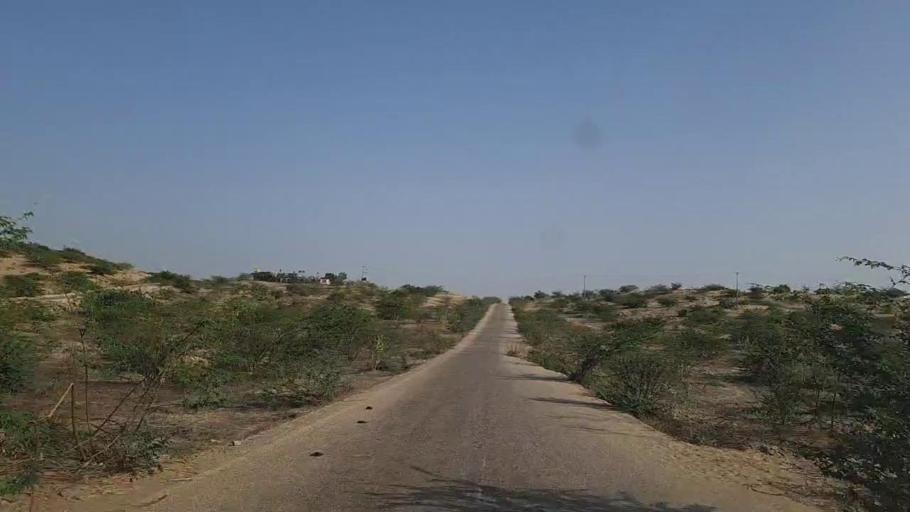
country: PK
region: Sindh
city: Naukot
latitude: 24.6255
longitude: 69.3671
